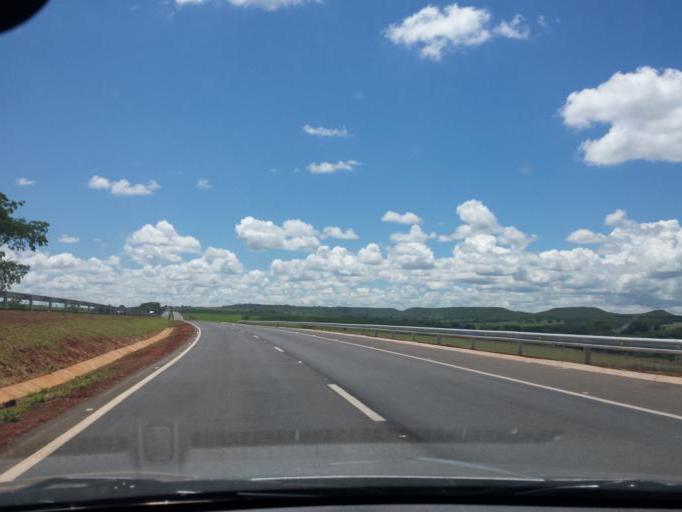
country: BR
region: Goias
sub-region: Cristalina
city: Cristalina
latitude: -16.6045
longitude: -47.7702
